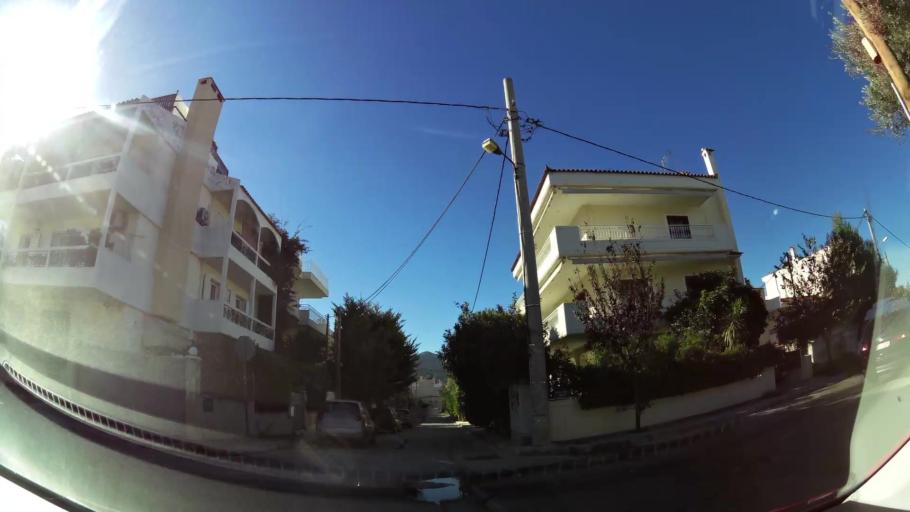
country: GR
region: Attica
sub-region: Nomarchia Athinas
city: Agia Paraskevi
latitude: 38.0196
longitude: 23.8439
